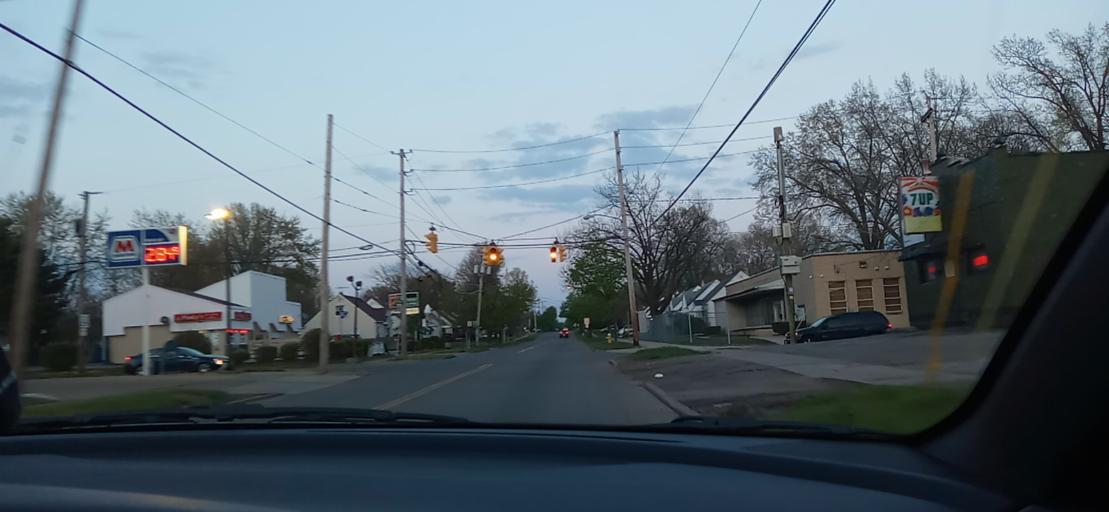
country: US
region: Ohio
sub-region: Summit County
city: Akron
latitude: 41.0468
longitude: -81.5007
